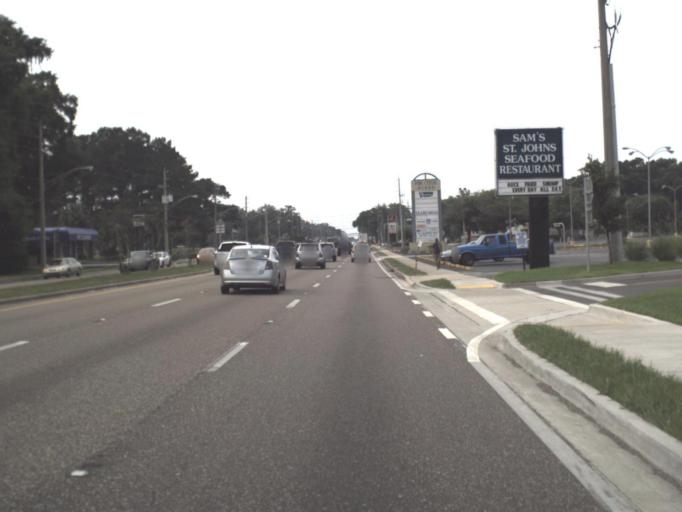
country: US
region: Florida
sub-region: Clay County
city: Orange Park
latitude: 30.1727
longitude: -81.7015
